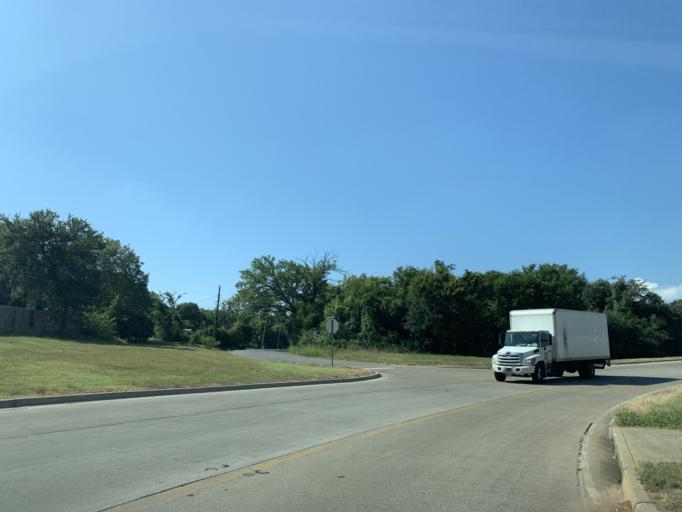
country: US
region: Texas
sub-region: Tarrant County
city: Azle
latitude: 32.8672
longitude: -97.5216
